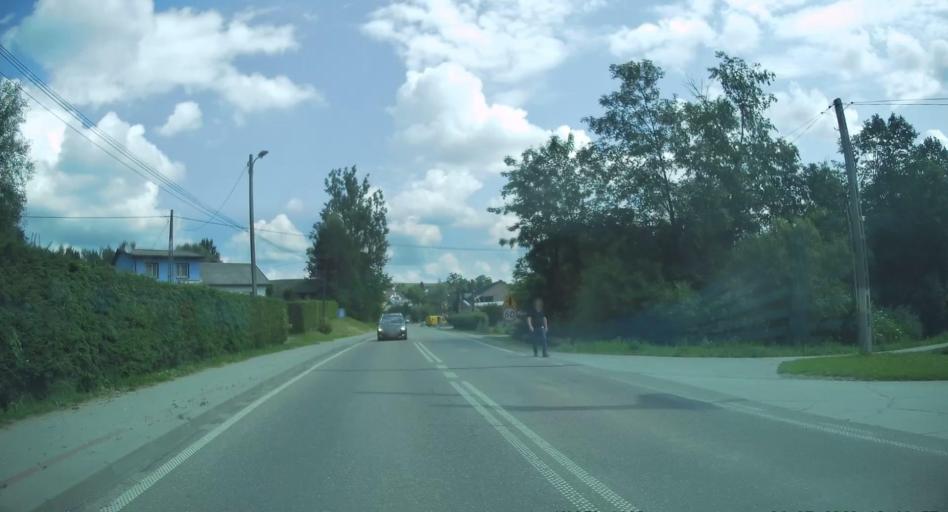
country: PL
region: Lesser Poland Voivodeship
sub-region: Powiat nowosadecki
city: Korzenna
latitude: 49.6722
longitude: 20.7769
